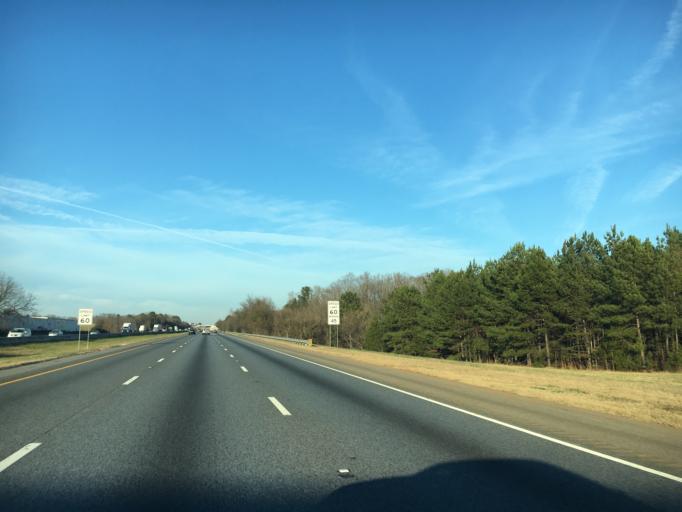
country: US
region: South Carolina
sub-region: Greenville County
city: Golden Grove
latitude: 34.7416
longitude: -82.4838
